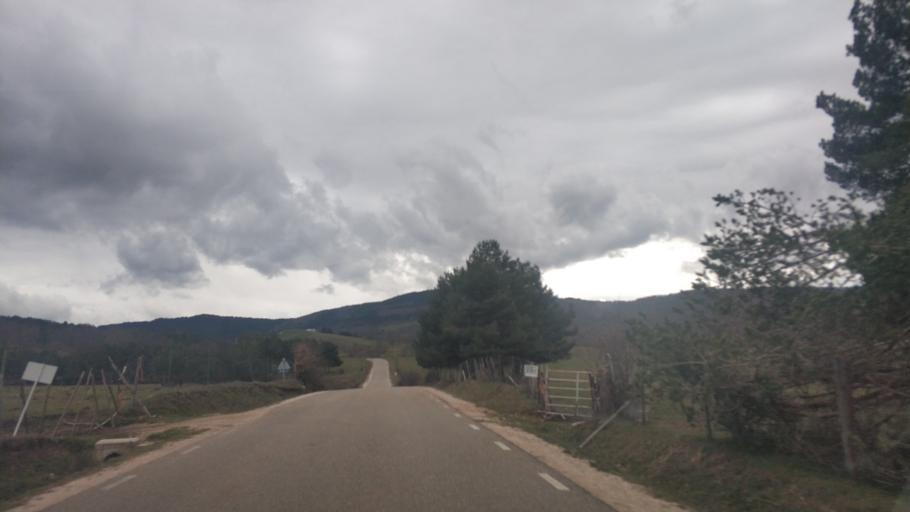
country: ES
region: Castille and Leon
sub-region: Provincia de Burgos
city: Canicosa de la Sierra
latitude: 41.9494
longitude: -3.0282
